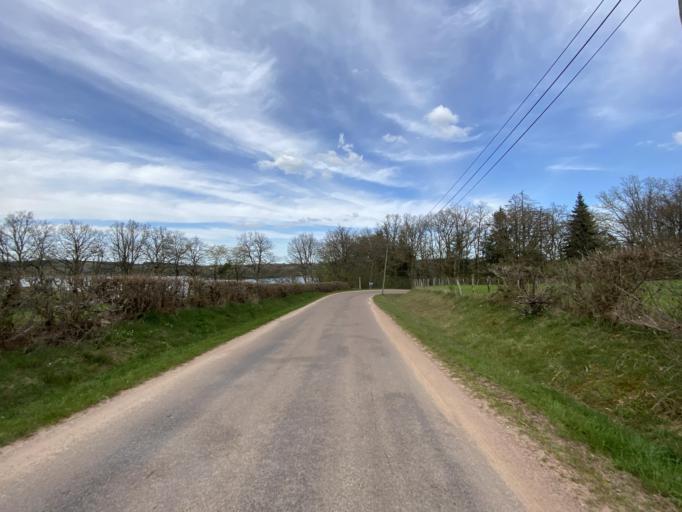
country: FR
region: Bourgogne
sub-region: Departement de la Cote-d'Or
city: Saulieu
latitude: 47.3200
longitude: 4.0932
